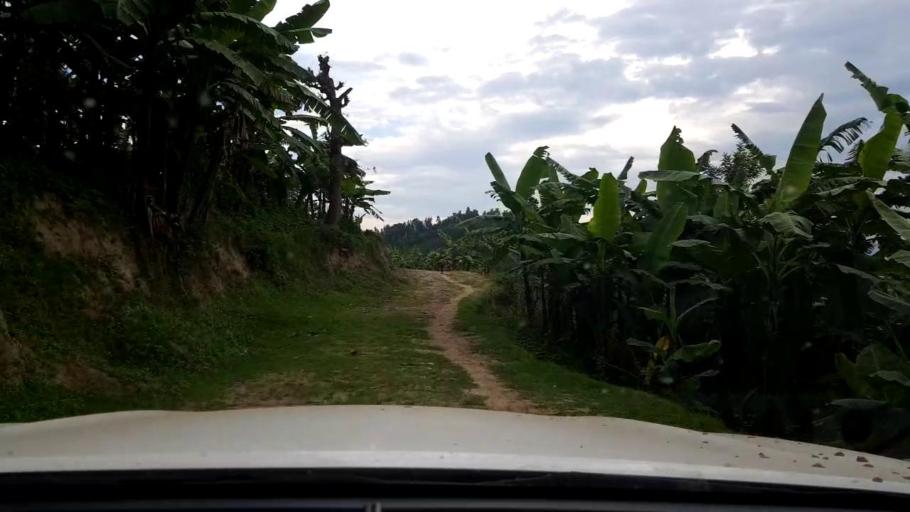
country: RW
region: Western Province
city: Kibuye
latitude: -1.9963
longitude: 29.3691
